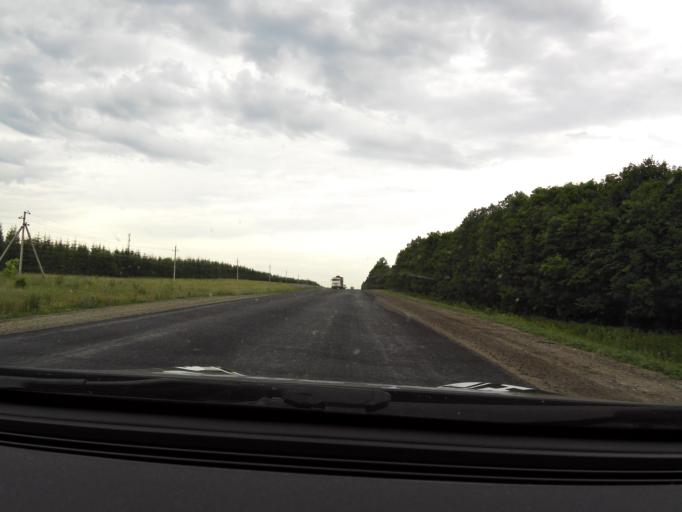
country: RU
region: Bashkortostan
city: Kudeyevskiy
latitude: 54.8064
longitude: 56.6290
